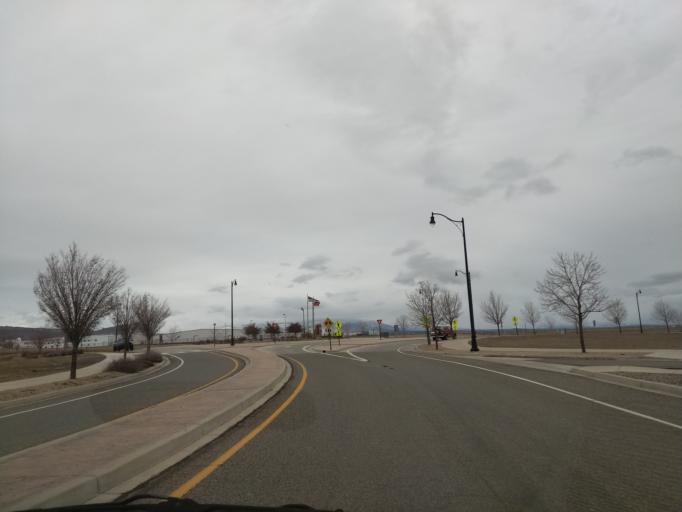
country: US
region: Colorado
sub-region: Mesa County
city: Fruitvale
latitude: 39.1185
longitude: -108.5310
